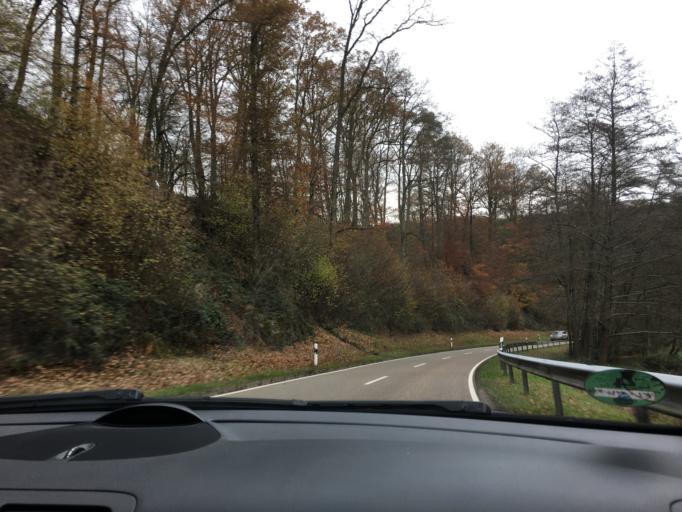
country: DE
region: Rheinland-Pfalz
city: Waldfischbach-Burgalben
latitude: 49.2995
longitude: 7.6634
